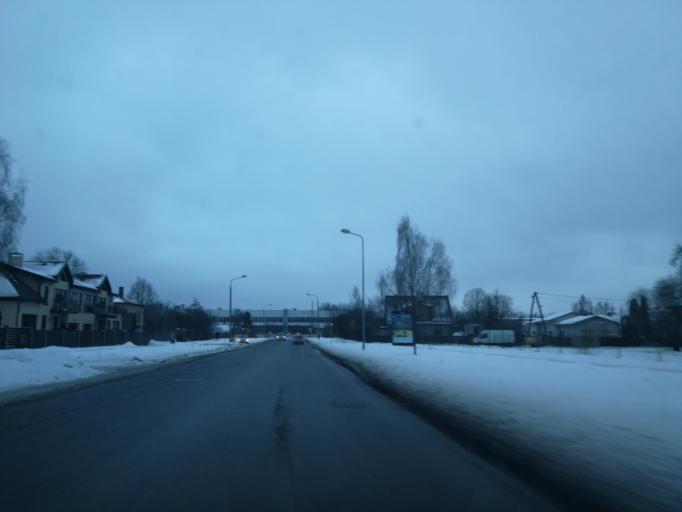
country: LV
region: Riga
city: Riga
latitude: 56.9425
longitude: 24.1748
